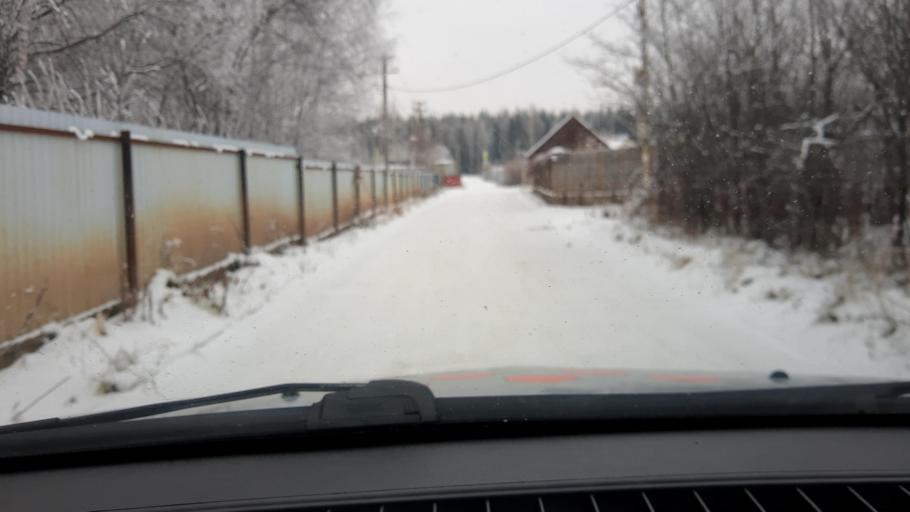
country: RU
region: Bashkortostan
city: Iglino
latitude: 54.8344
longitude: 56.2242
